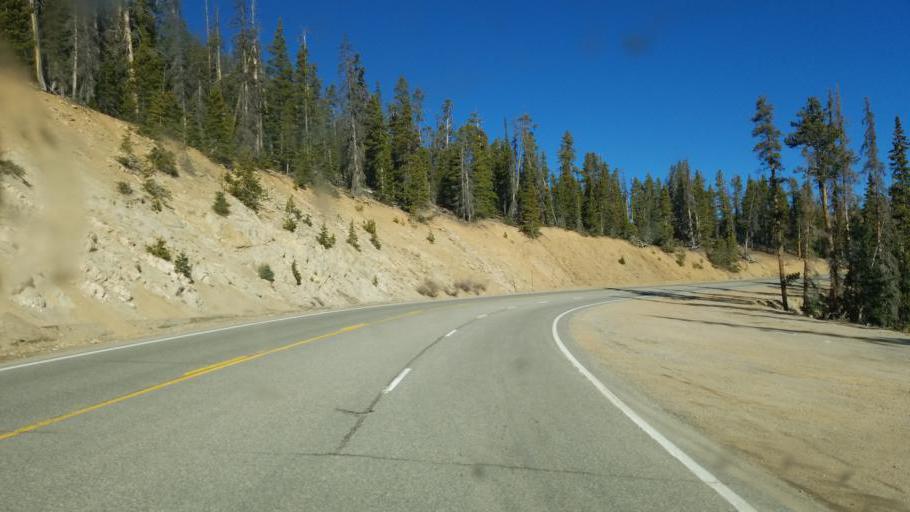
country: US
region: Colorado
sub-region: Chaffee County
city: Salida
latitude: 38.4839
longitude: -106.3398
